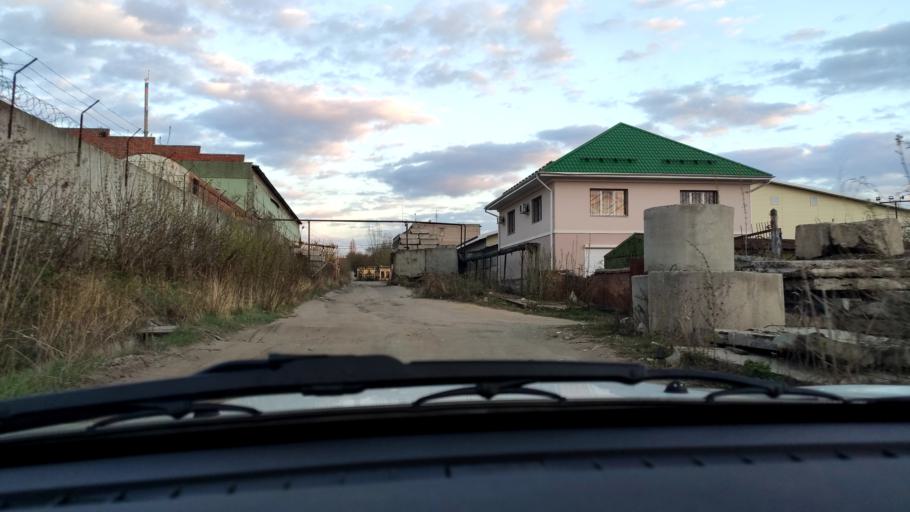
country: RU
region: Voronezj
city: Voronezh
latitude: 51.6868
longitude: 39.1452
